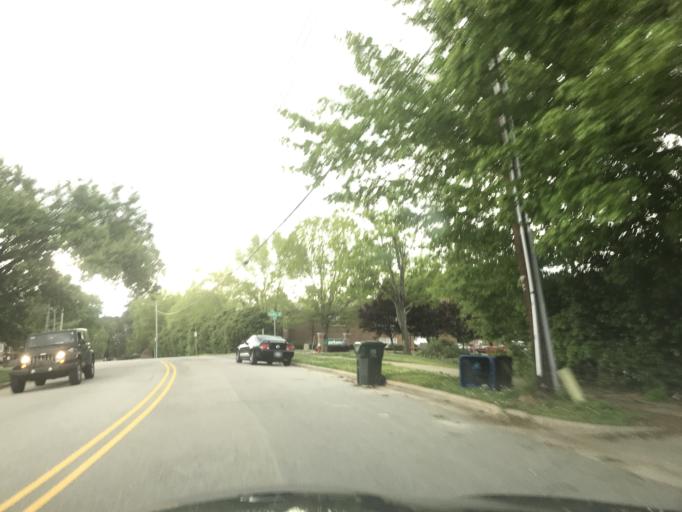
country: US
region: North Carolina
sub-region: Wake County
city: West Raleigh
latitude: 35.7747
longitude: -78.6855
